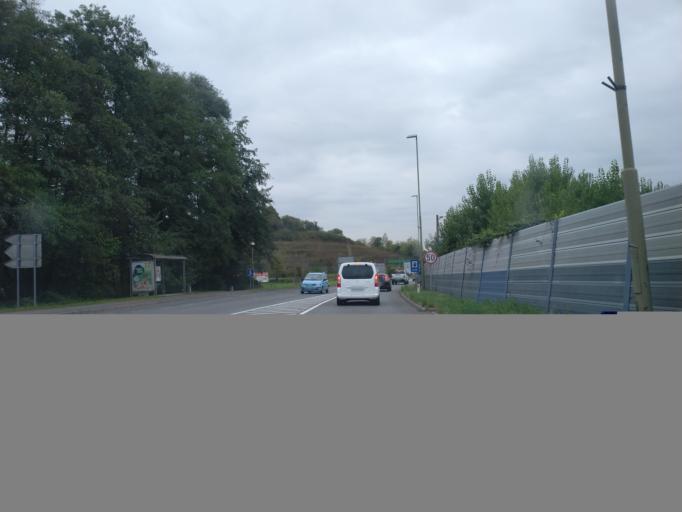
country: SI
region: Sempeter-Vrtojba
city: Sempeter pri Gorici
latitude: 45.9415
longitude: 13.6423
